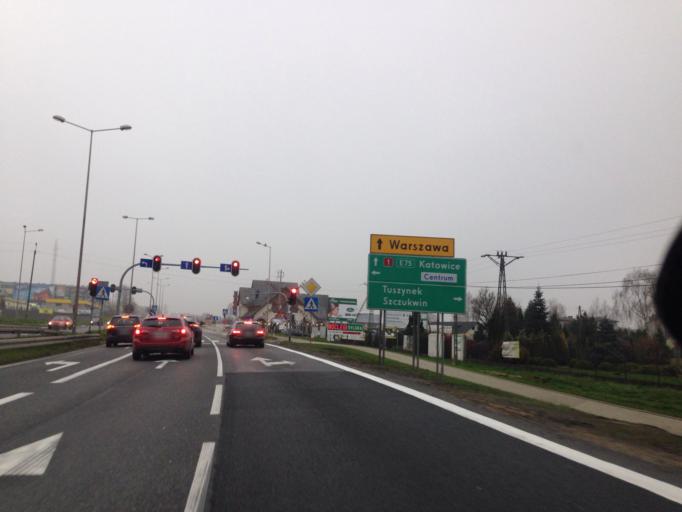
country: PL
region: Lodz Voivodeship
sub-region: Powiat lodzki wschodni
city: Tuszyn
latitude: 51.6004
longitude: 19.5416
